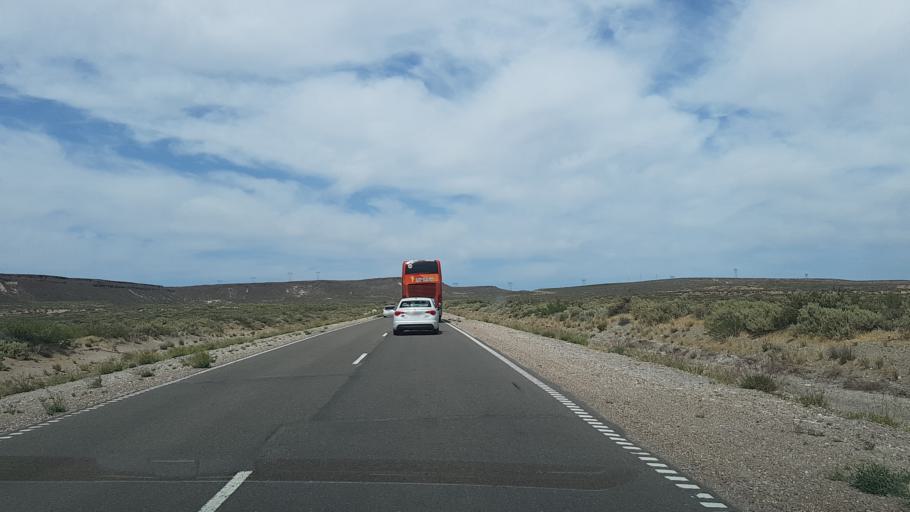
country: AR
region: Neuquen
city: Piedra del Aguila
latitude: -39.9663
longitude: -70.0114
